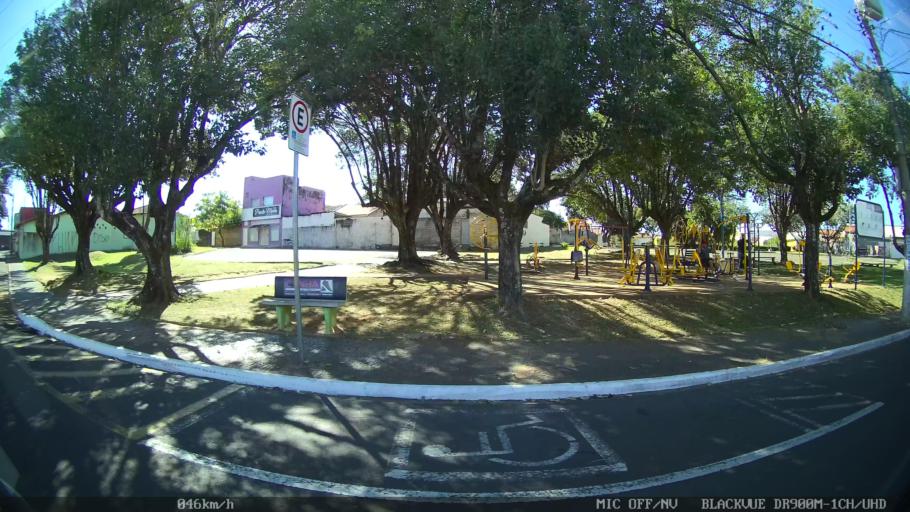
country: BR
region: Sao Paulo
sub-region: Franca
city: Franca
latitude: -20.5285
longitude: -47.3685
